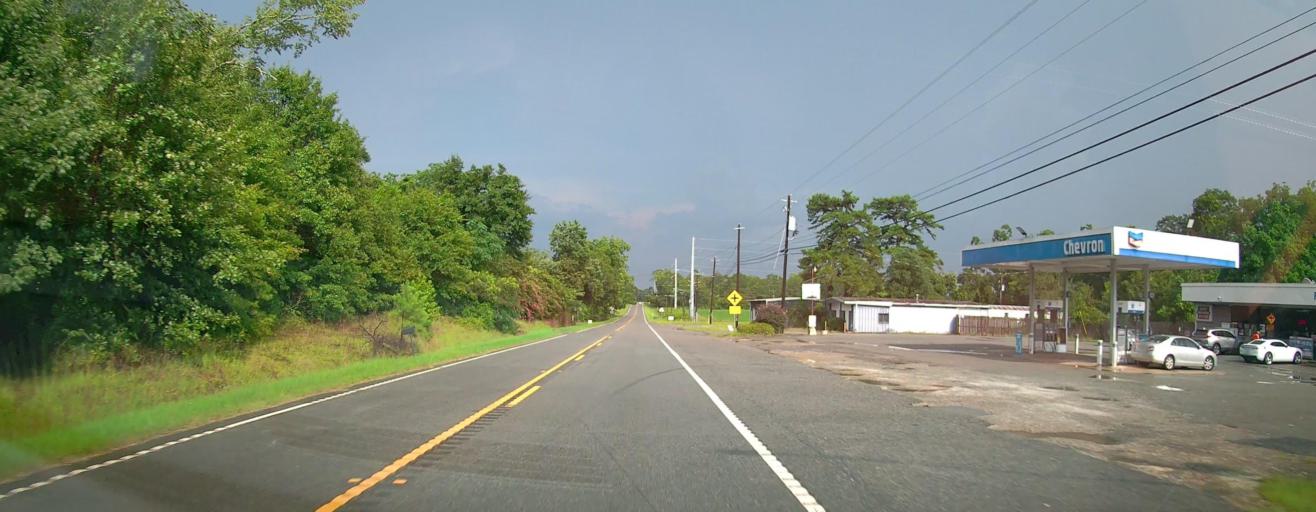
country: US
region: Georgia
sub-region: Twiggs County
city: Jeffersonville
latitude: 32.6036
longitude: -83.2490
